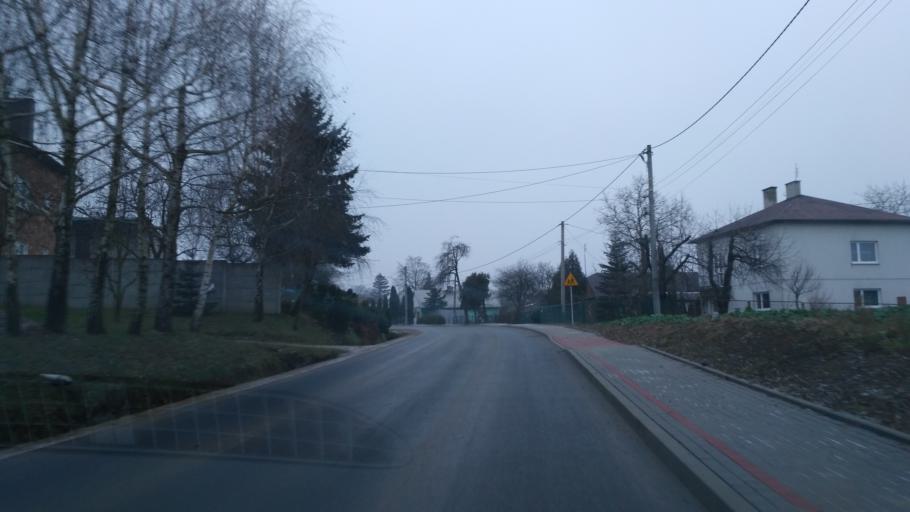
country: PL
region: Subcarpathian Voivodeship
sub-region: Powiat przeworski
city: Kanczuga
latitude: 50.0156
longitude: 22.4143
